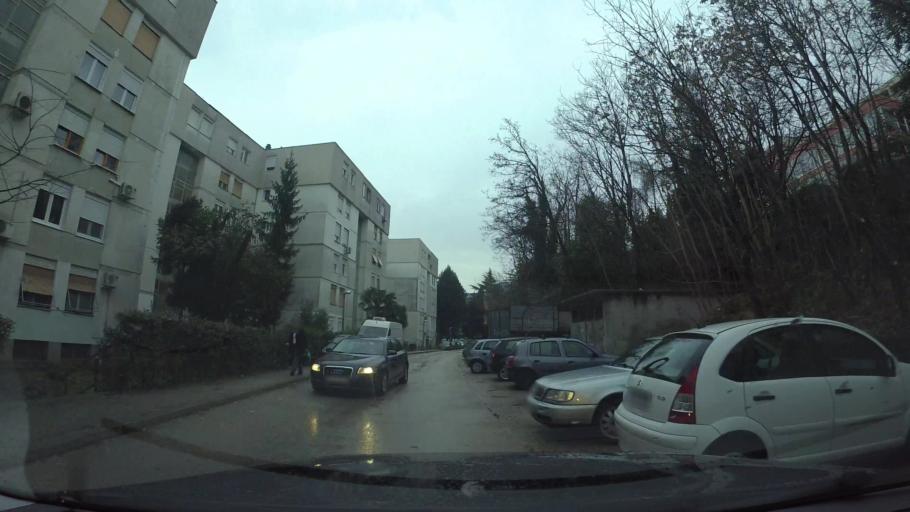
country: BA
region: Federation of Bosnia and Herzegovina
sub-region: Hercegovacko-Bosanski Kanton
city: Mostar
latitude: 43.3485
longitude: 17.7960
